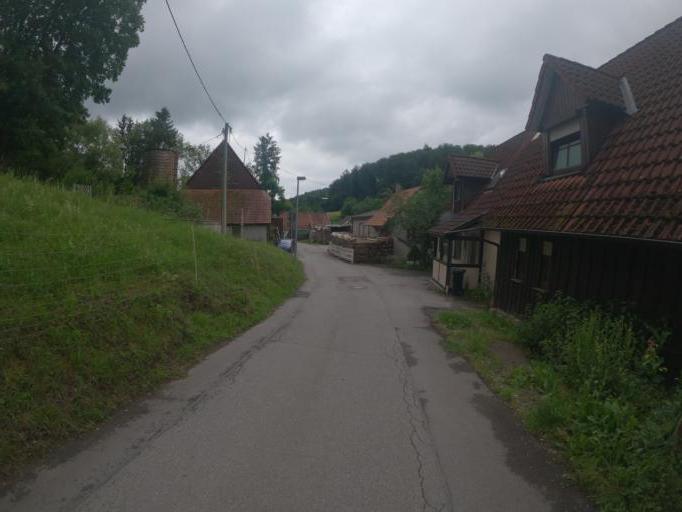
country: DE
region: Baden-Wuerttemberg
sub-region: Regierungsbezirk Stuttgart
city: Ebersbach an der Fils
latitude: 48.7431
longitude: 9.5419
